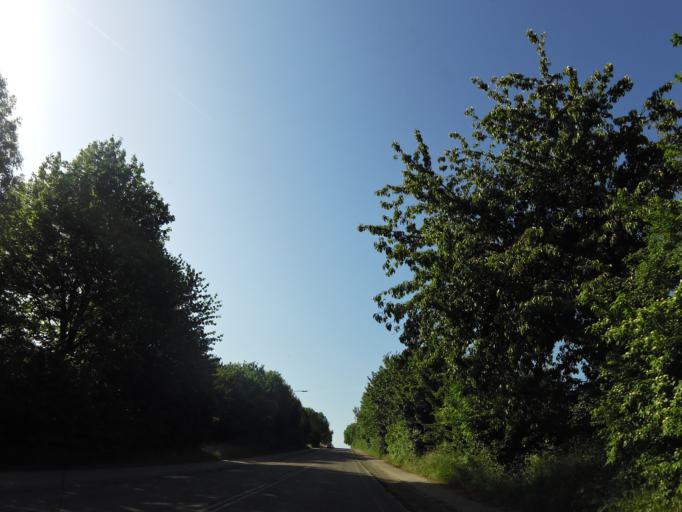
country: NL
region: Limburg
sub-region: Gemeente Voerendaal
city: Kunrade
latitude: 50.8707
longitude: 5.9355
